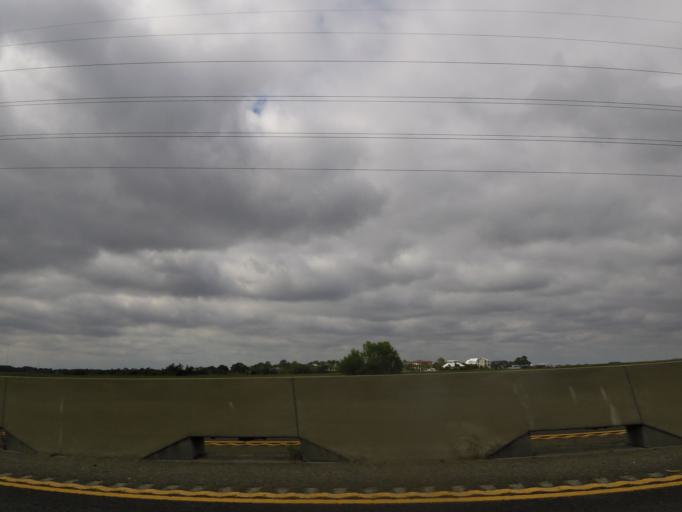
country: US
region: Georgia
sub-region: Glynn County
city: Brunswick
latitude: 31.1629
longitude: -81.4531
